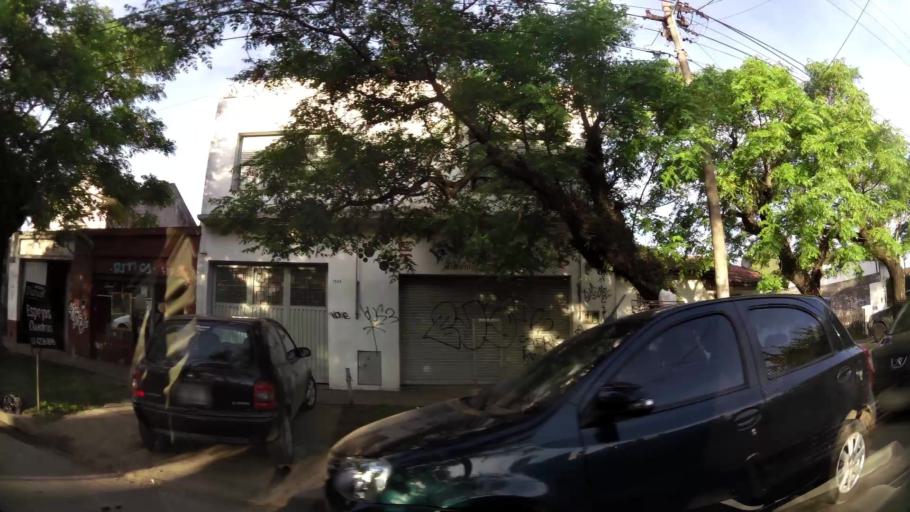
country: AR
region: Buenos Aires
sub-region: Partido de Almirante Brown
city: Adrogue
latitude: -34.7959
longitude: -58.3571
